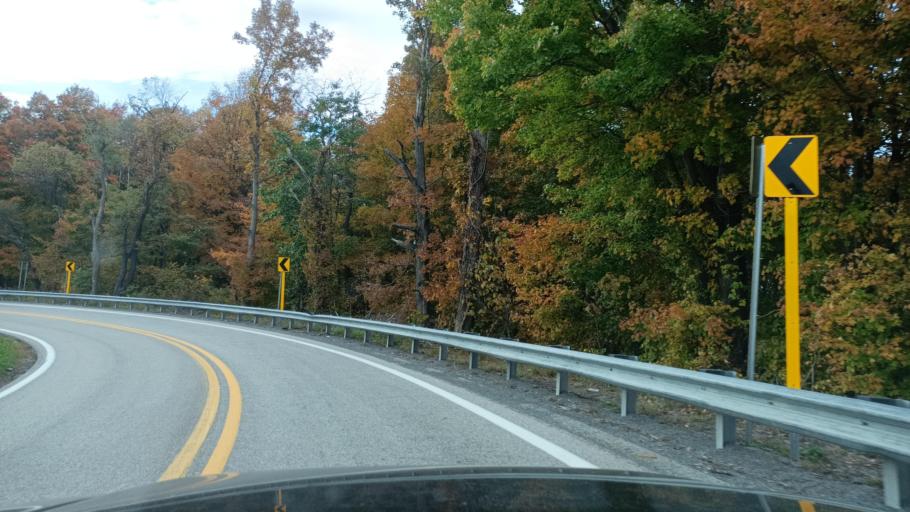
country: US
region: West Virginia
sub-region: Preston County
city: Kingwood
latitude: 39.3351
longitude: -79.7673
